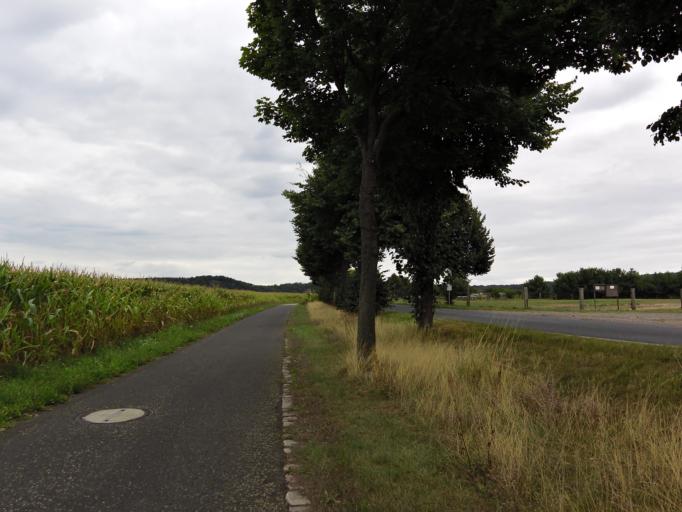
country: DE
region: Saxony
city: Weissig
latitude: 51.2153
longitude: 13.4090
